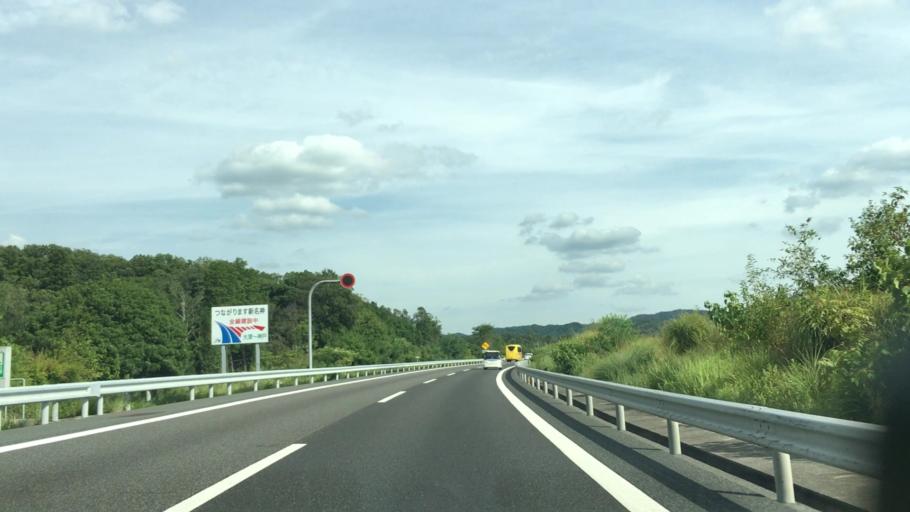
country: JP
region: Shiga Prefecture
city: Kusatsu
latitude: 34.9619
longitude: 135.9700
